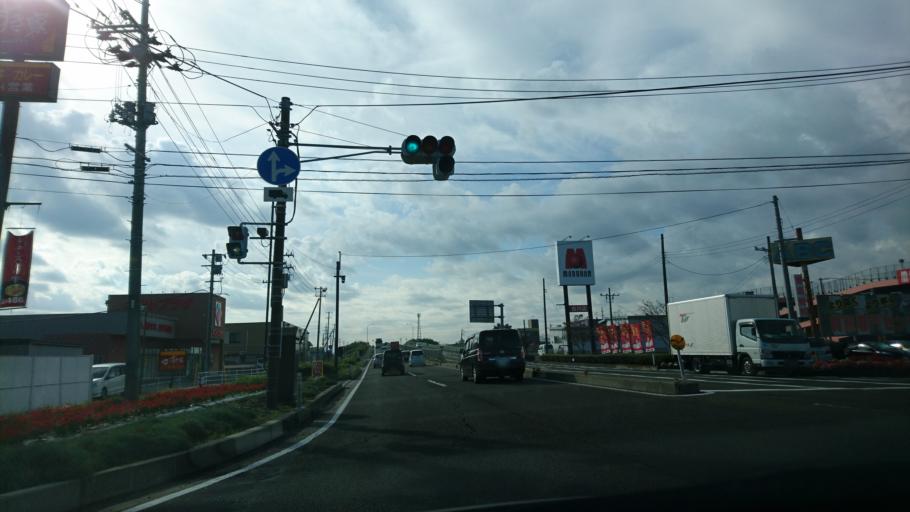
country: JP
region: Miyagi
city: Furukawa
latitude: 38.5744
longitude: 140.9465
